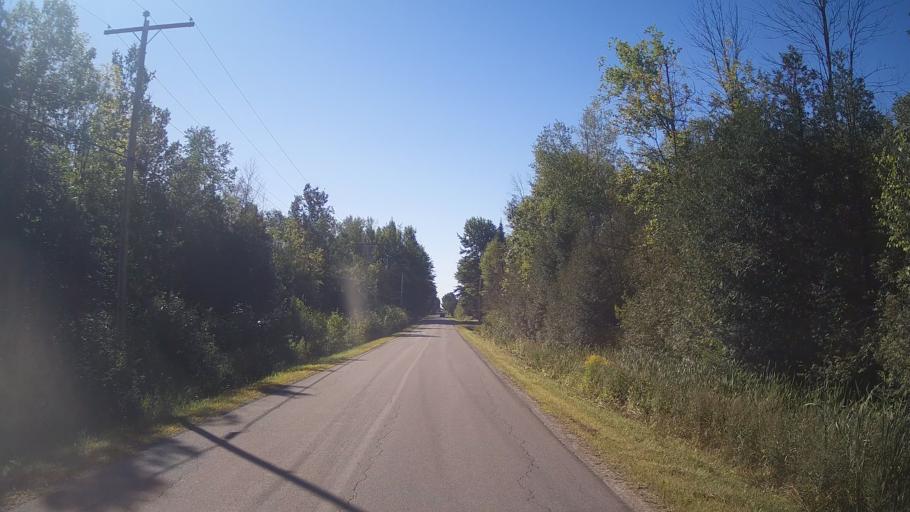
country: CA
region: Ontario
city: Prescott
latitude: 45.0160
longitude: -75.6141
